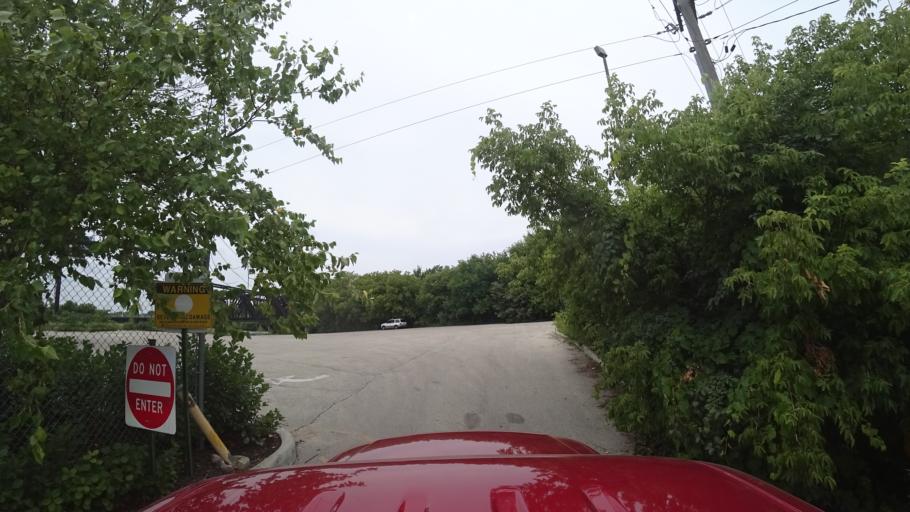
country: US
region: Illinois
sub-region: Cook County
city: Chicago
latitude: 41.8369
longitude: -87.6853
